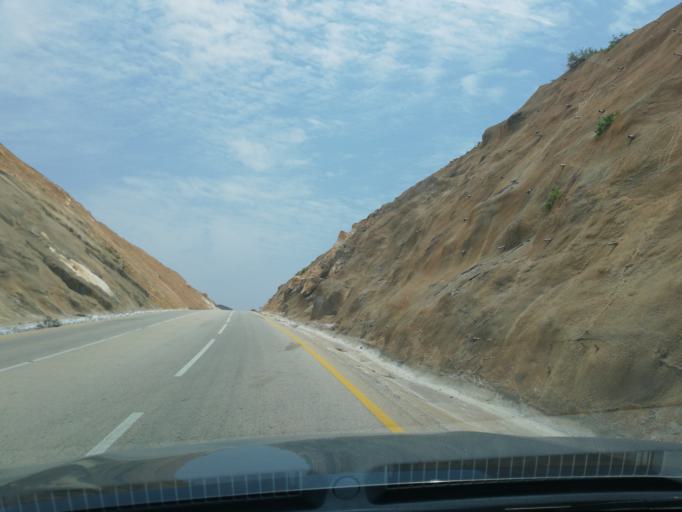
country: OM
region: Zufar
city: Salalah
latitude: 16.8745
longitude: 53.7289
